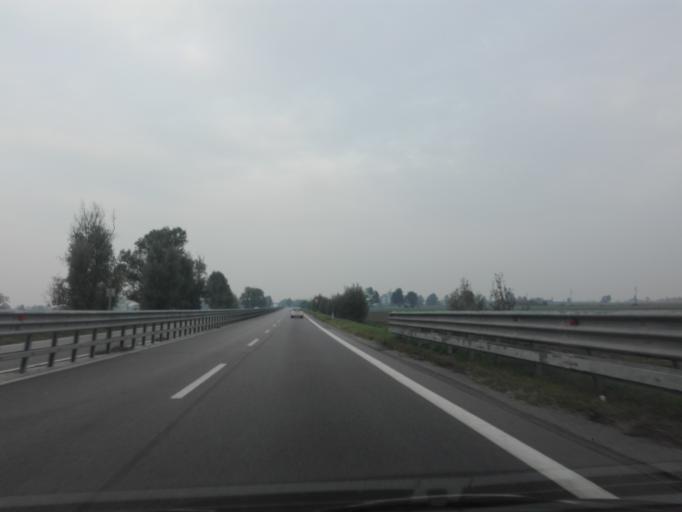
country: IT
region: Veneto
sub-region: Provincia di Rovigo
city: Fratta Polesine
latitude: 45.0224
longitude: 11.6343
